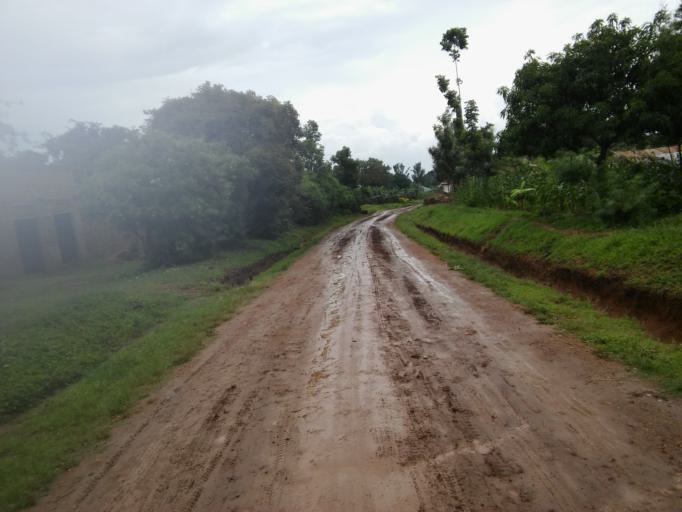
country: UG
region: Eastern Region
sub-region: Mbale District
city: Mbale
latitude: 1.0326
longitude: 34.1996
